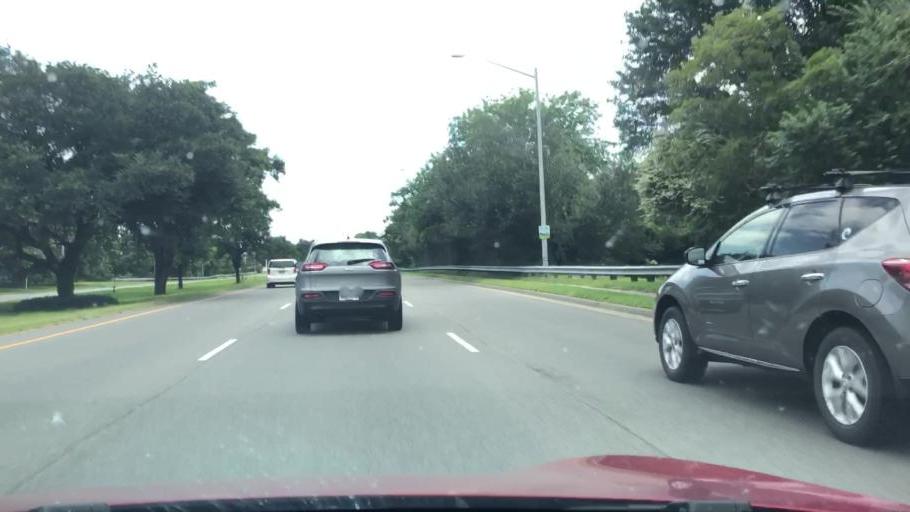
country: US
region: Virginia
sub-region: City of Chesapeake
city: Chesapeake
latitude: 36.8583
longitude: -76.1334
